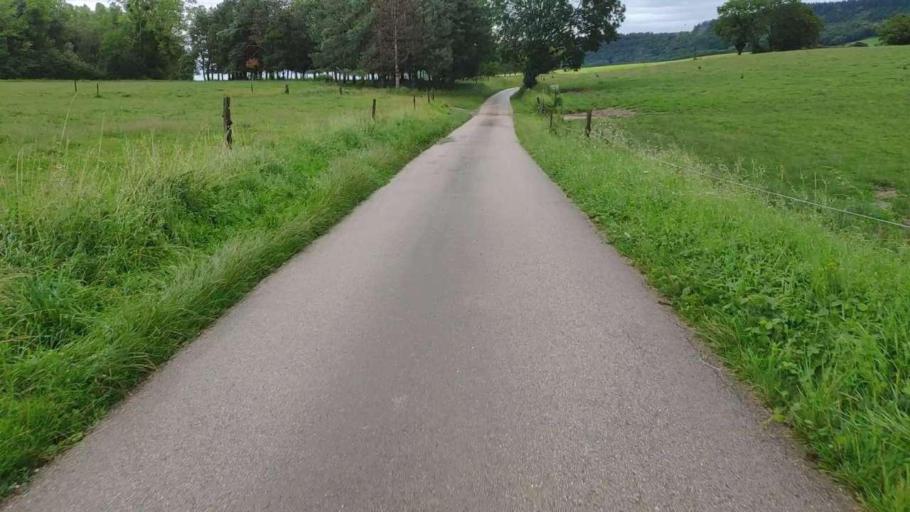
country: FR
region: Franche-Comte
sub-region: Departement du Jura
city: Poligny
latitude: 46.7854
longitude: 5.6042
